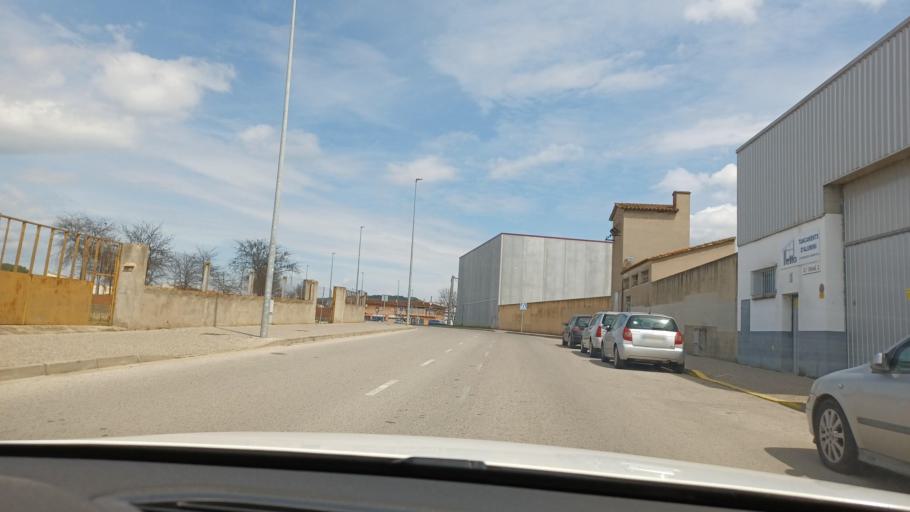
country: ES
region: Catalonia
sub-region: Provincia de Girona
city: Sarria de Ter
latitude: 42.0140
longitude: 2.8216
